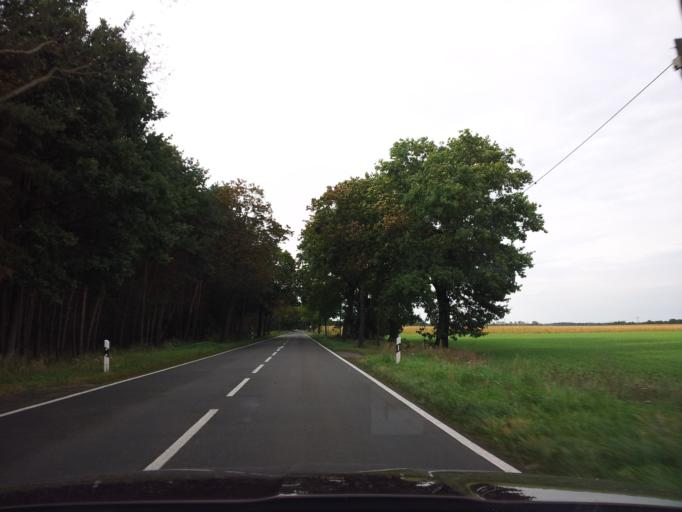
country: DE
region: Brandenburg
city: Treuenbrietzen
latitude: 52.0933
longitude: 12.9470
